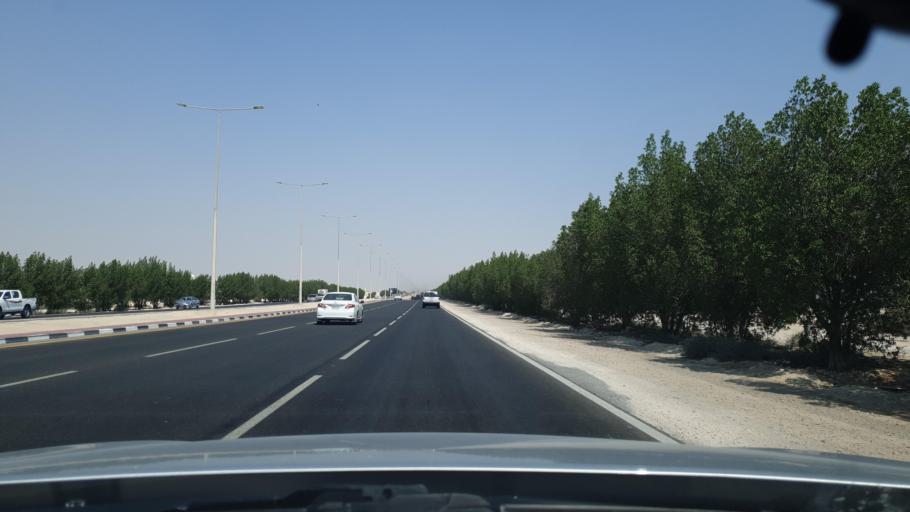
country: QA
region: Al Khawr
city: Al Khawr
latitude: 25.6944
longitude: 51.5016
